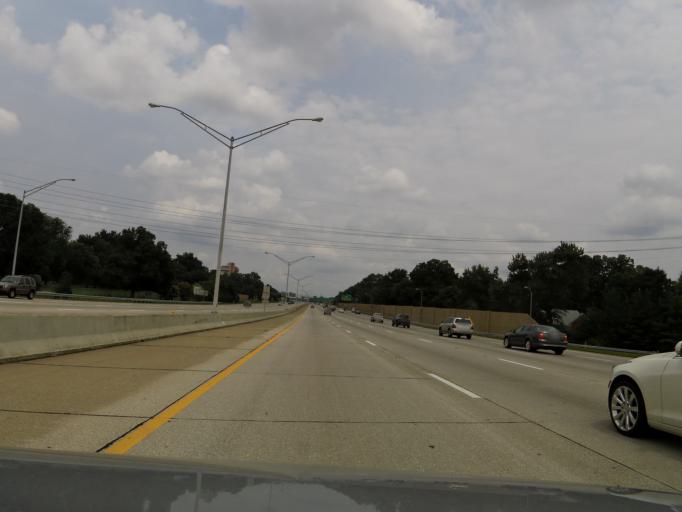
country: US
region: Kentucky
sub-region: Jefferson County
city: Buechel
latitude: 38.2229
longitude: -85.6477
